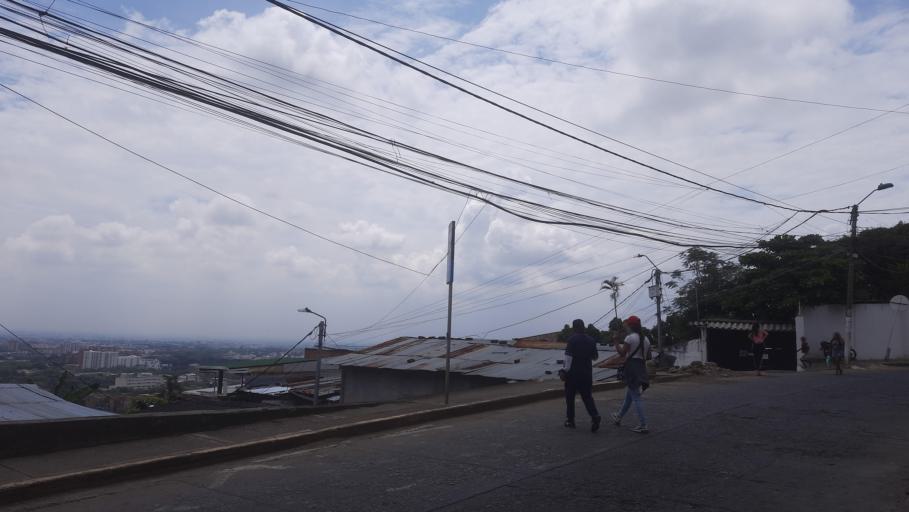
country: CO
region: Valle del Cauca
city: Cali
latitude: 3.3734
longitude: -76.5548
